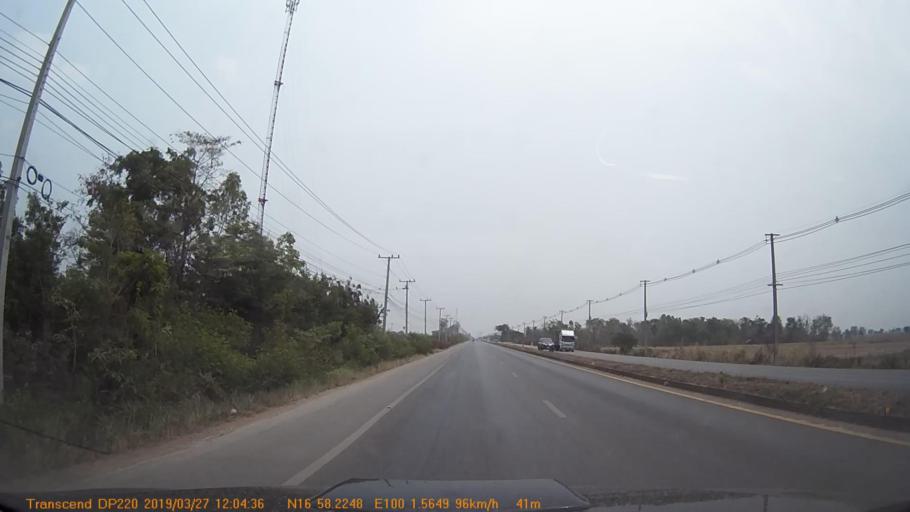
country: TH
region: Sukhothai
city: Kong Krailat
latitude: 16.9704
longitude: 100.0264
